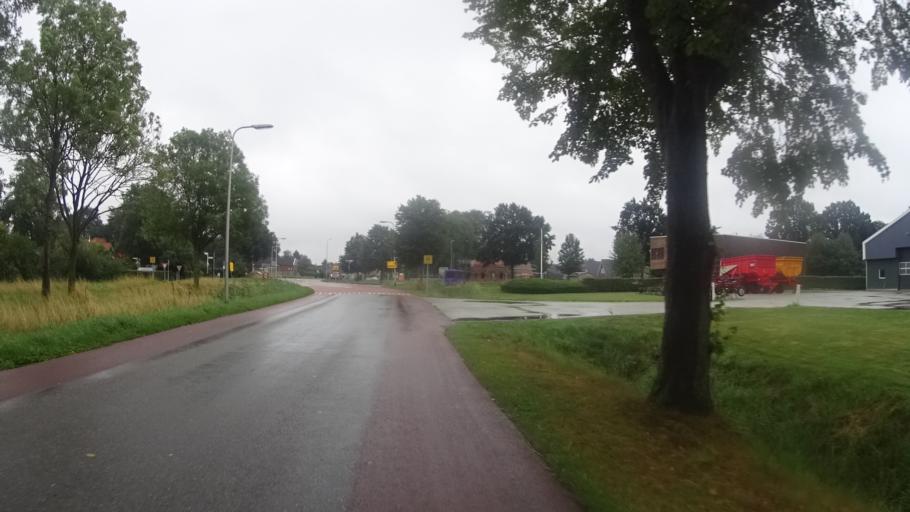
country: NL
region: Groningen
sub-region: Gemeente  Oldambt
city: Winschoten
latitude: 53.1800
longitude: 6.9632
